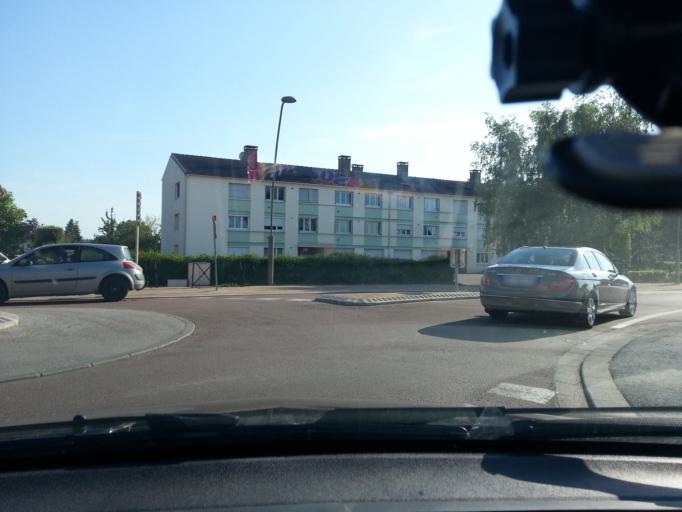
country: FR
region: Bourgogne
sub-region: Departement de Saone-et-Loire
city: Saint-Marcel
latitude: 46.7764
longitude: 4.8860
